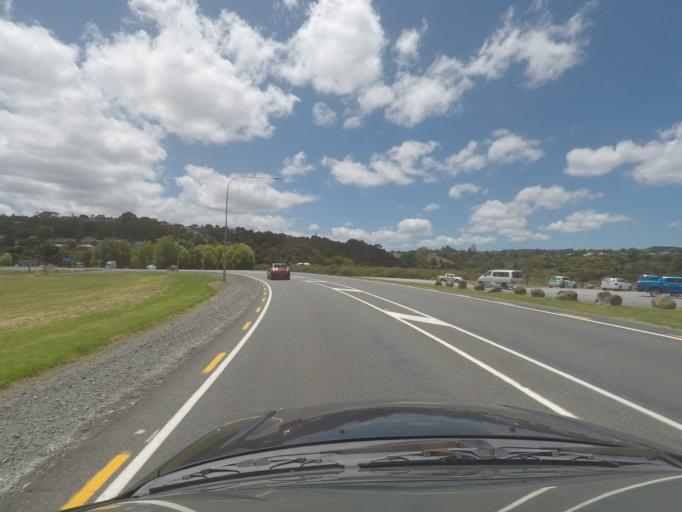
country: NZ
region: Northland
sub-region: Whangarei
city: Whangarei
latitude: -35.7337
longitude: 174.3426
